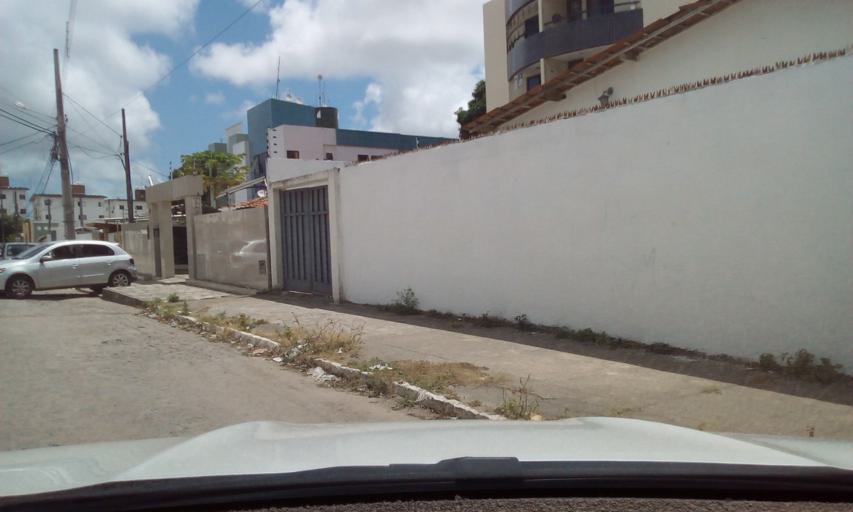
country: BR
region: Paraiba
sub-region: Joao Pessoa
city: Joao Pessoa
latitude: -7.1818
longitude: -34.8658
